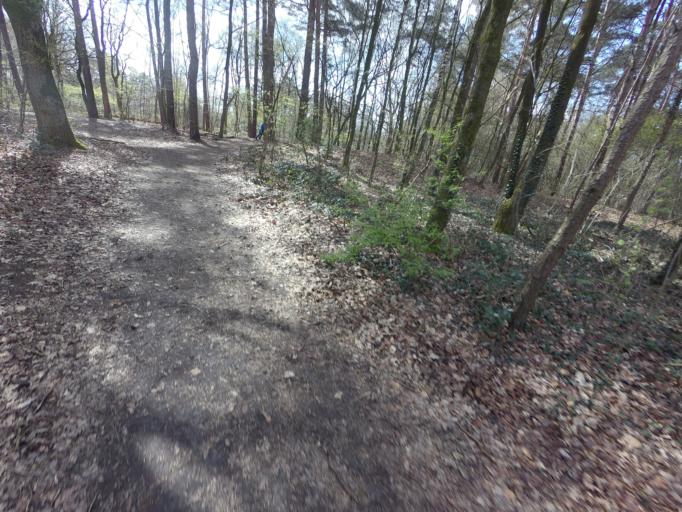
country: NL
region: Limburg
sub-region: Gemeente Roerdalen
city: Herkenbosch
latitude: 51.1645
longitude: 6.0898
